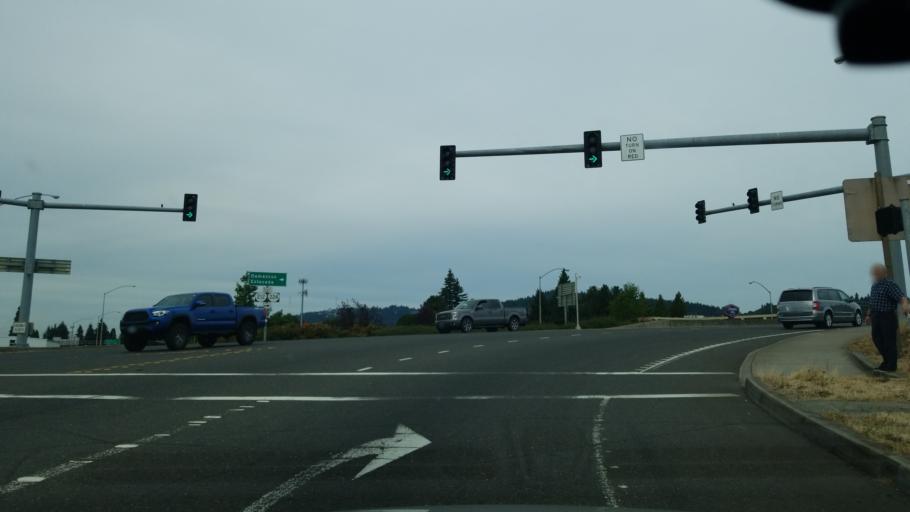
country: US
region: Oregon
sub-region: Clackamas County
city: Clackamas
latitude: 45.4071
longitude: -122.5724
